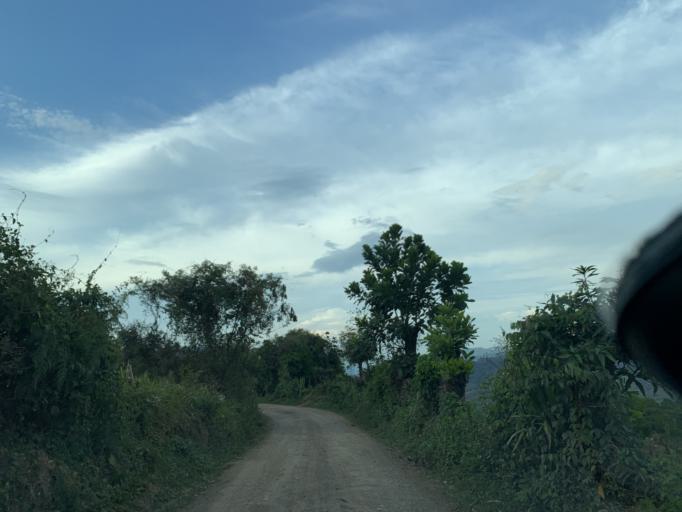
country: CO
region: Boyaca
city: Santana
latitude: 6.0858
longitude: -73.4959
